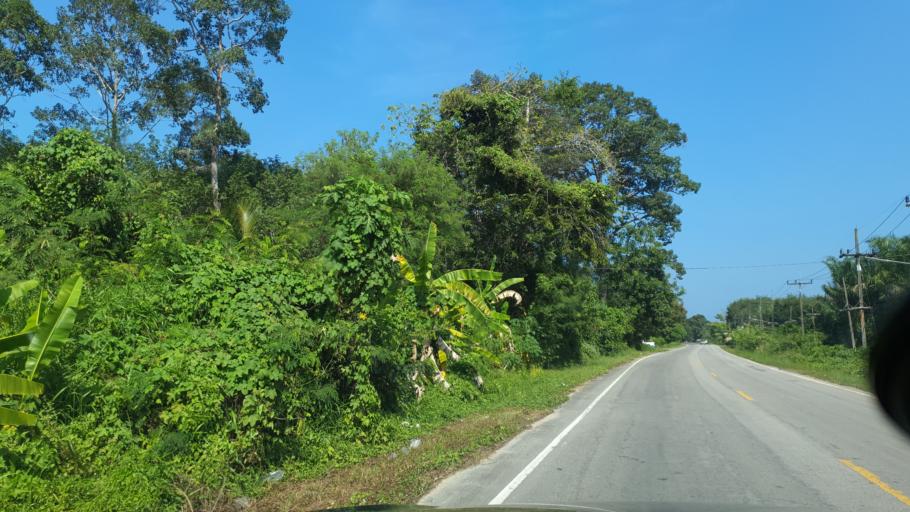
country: TH
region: Surat Thani
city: Tha Chana
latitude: 9.5741
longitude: 99.1810
